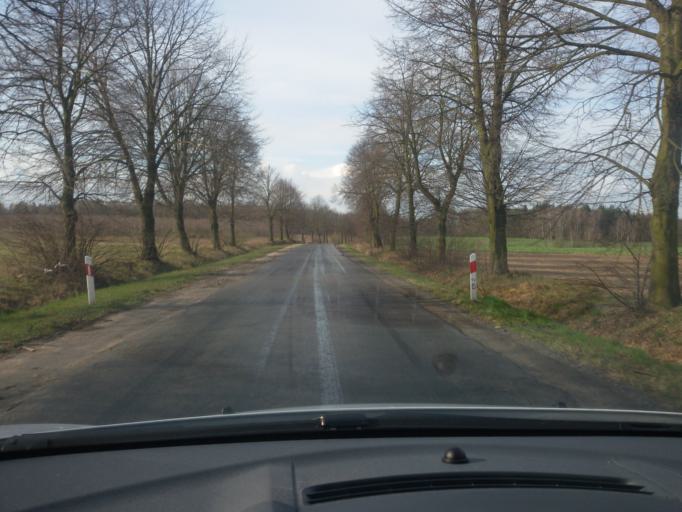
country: PL
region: Lubusz
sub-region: Powiat nowosolski
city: Nowe Miasteczko
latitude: 51.7069
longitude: 15.7484
